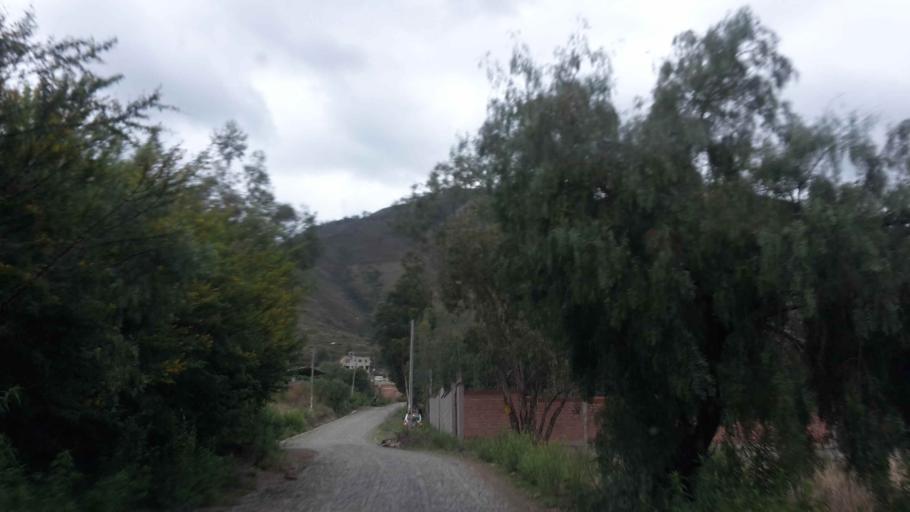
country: BO
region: Cochabamba
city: Cochabamba
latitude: -17.3771
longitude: -66.0563
